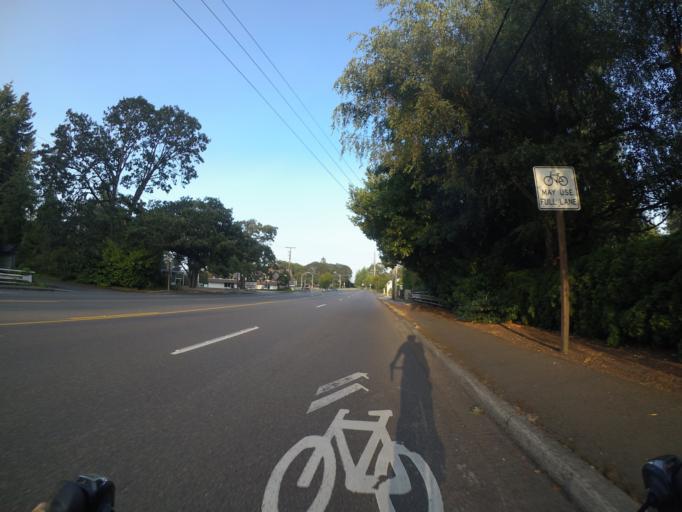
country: US
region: Washington
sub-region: Pierce County
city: Lakewood
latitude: 47.1557
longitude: -122.5232
